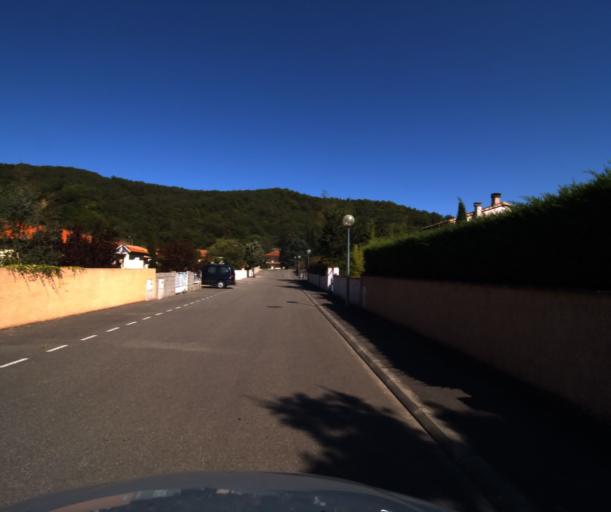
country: FR
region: Midi-Pyrenees
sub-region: Departement de la Haute-Garonne
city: Le Fauga
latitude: 43.4210
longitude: 1.3154
